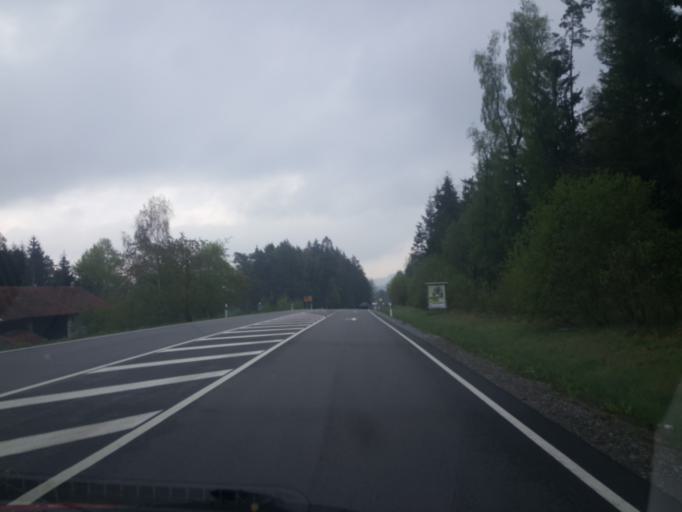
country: DE
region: Bavaria
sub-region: Lower Bavaria
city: Viechtach
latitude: 49.0650
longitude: 12.8989
